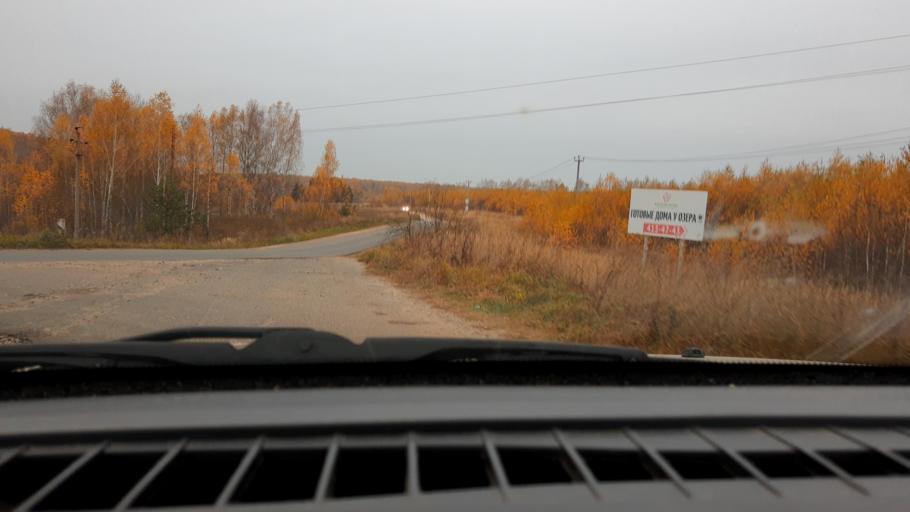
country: RU
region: Nizjnij Novgorod
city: Burevestnik
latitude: 56.0384
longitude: 43.8343
